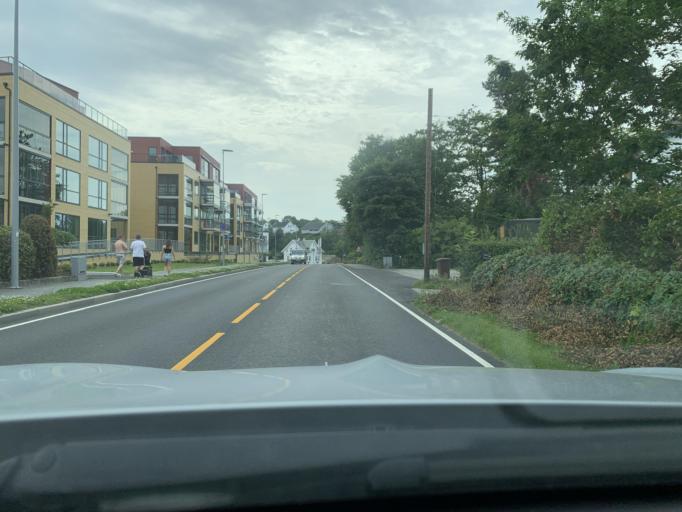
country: NO
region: Rogaland
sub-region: Sandnes
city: Sandnes
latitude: 58.7800
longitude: 5.7196
